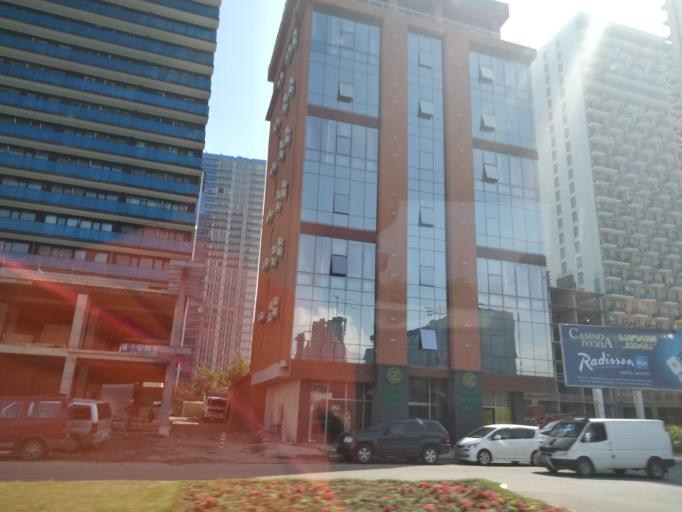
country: GE
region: Ajaria
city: Batumi
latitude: 41.6296
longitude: 41.6021
